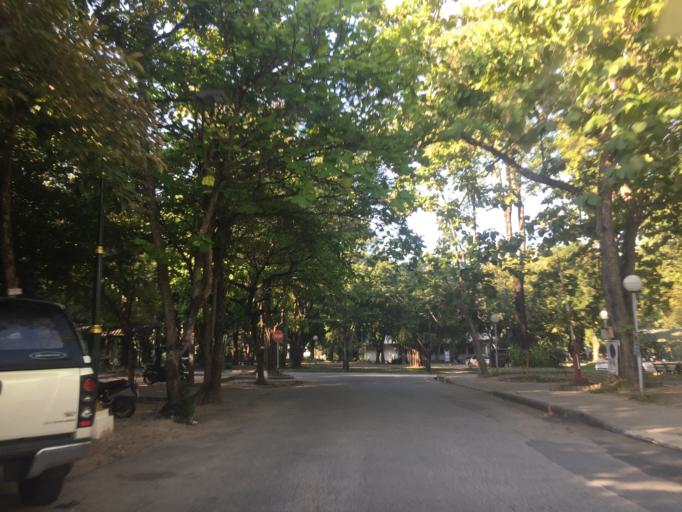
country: TH
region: Chiang Mai
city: Chiang Mai
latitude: 18.7991
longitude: 98.9552
